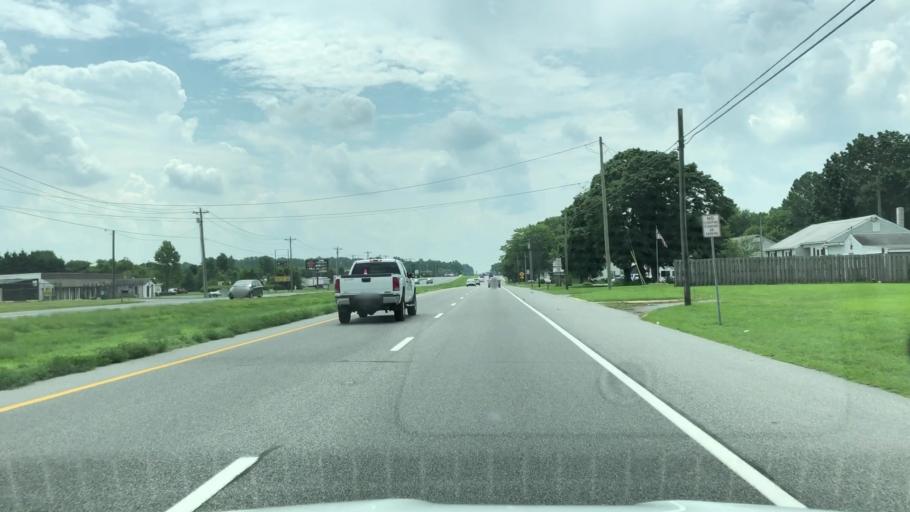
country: US
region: Delaware
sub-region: Kent County
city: Felton
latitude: 39.0283
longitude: -75.5628
